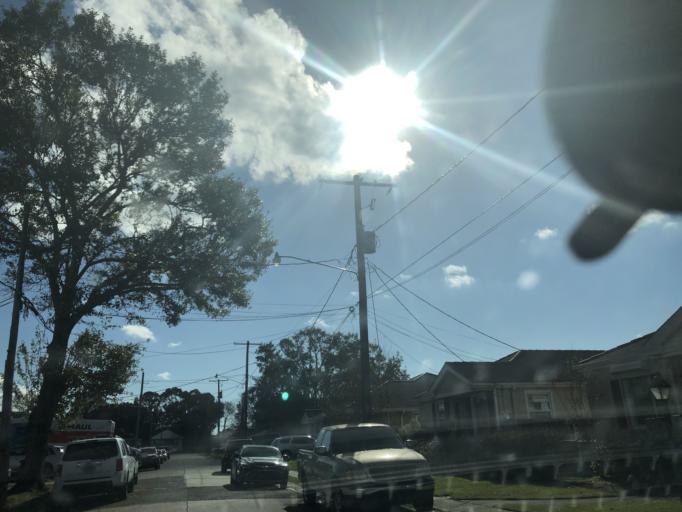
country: US
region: Louisiana
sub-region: Jefferson Parish
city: Metairie Terrace
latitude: 29.9796
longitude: -90.1592
